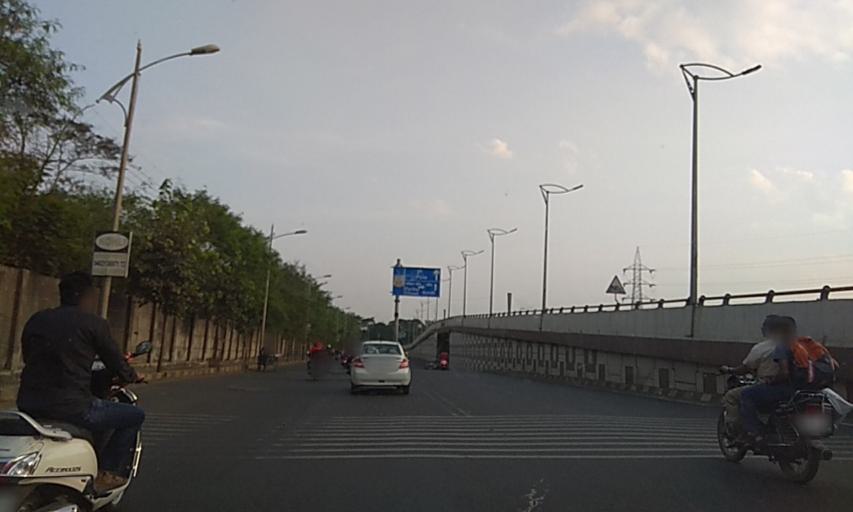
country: IN
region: Maharashtra
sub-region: Pune Division
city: Khadki
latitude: 18.5715
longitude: 73.8082
